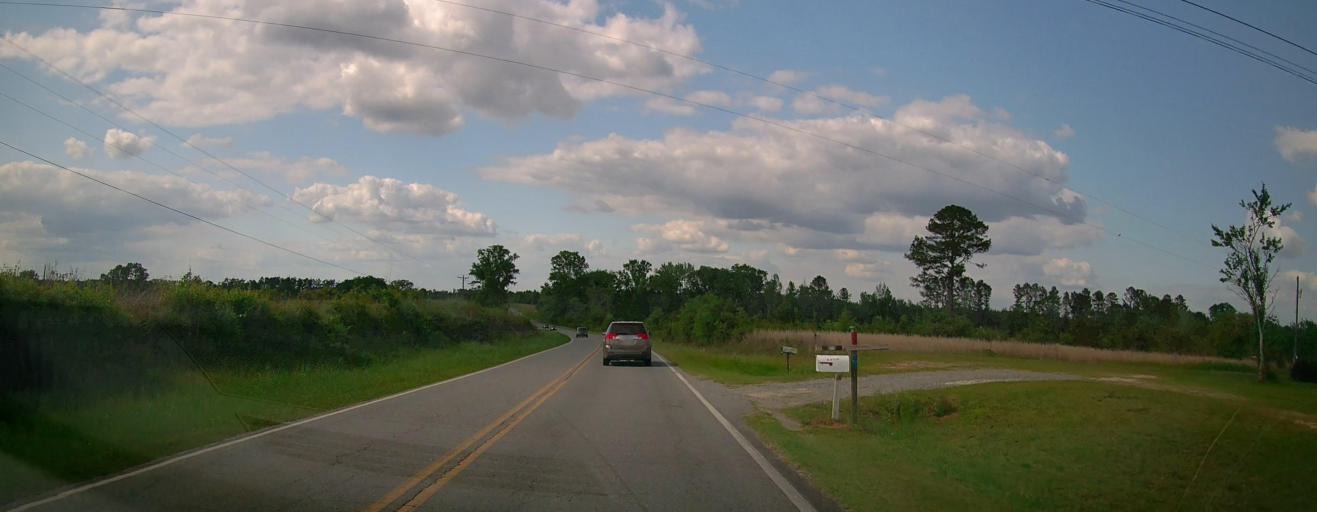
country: US
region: Georgia
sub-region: Laurens County
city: East Dublin
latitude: 32.6094
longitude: -82.8681
